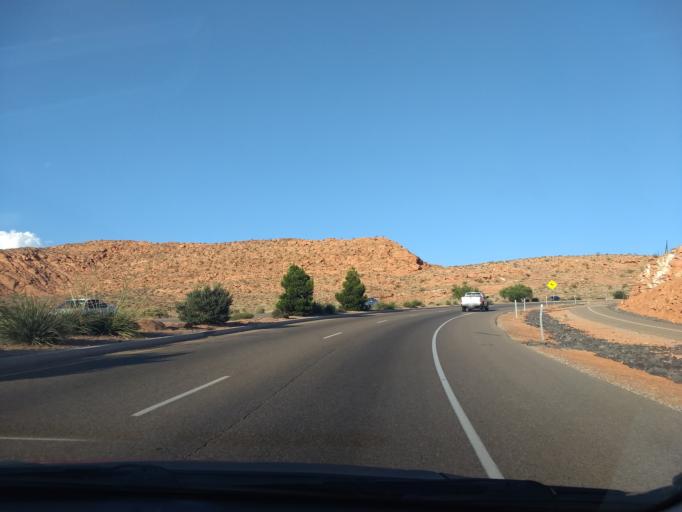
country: US
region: Utah
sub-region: Washington County
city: Saint George
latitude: 37.1359
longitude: -113.5996
